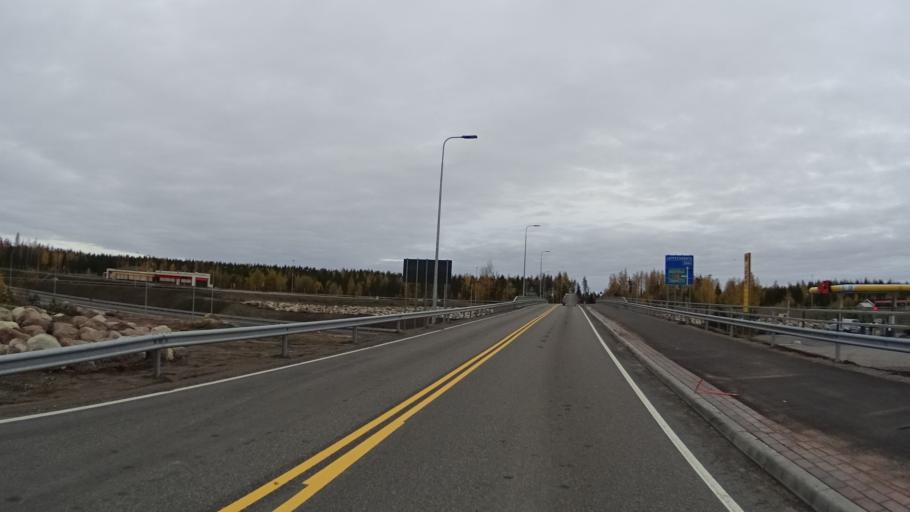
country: FI
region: South Karelia
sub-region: Lappeenranta
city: Luumaeki
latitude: 60.9278
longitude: 27.6311
